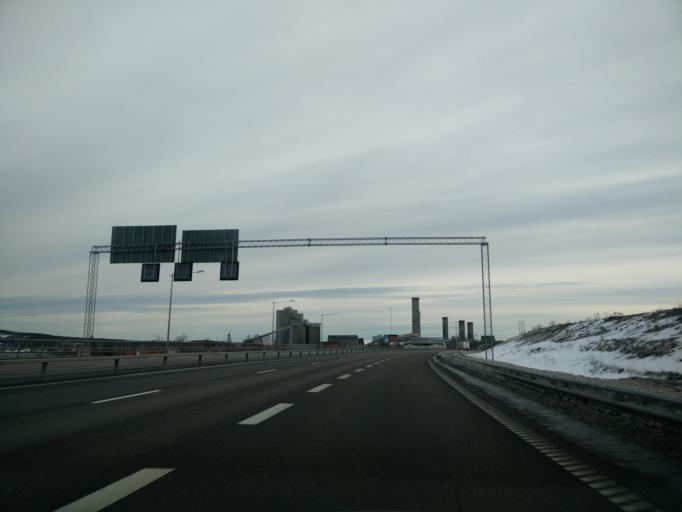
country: SE
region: Vaesternorrland
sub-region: Sundsvalls Kommun
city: Stockvik
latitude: 62.3775
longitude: 17.3608
